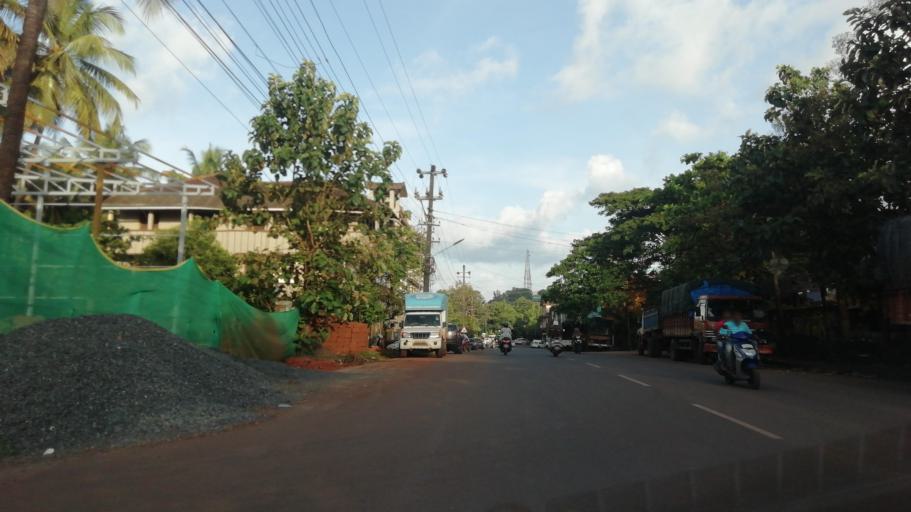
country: IN
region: Goa
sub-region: North Goa
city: Ponda
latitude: 15.3999
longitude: 74.0162
